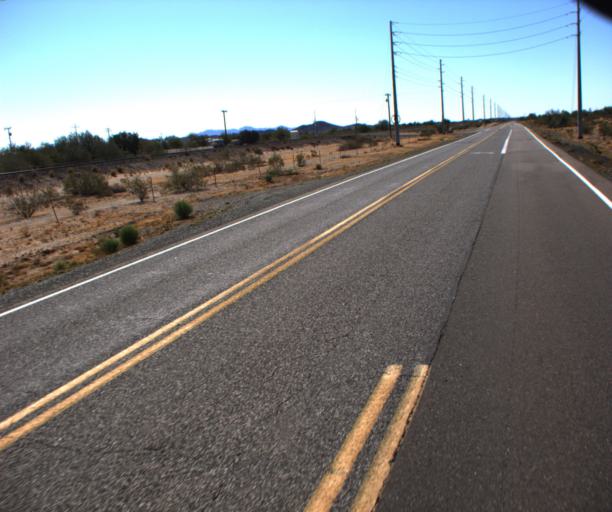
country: US
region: Arizona
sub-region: La Paz County
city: Cienega Springs
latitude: 33.9618
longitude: -114.0329
